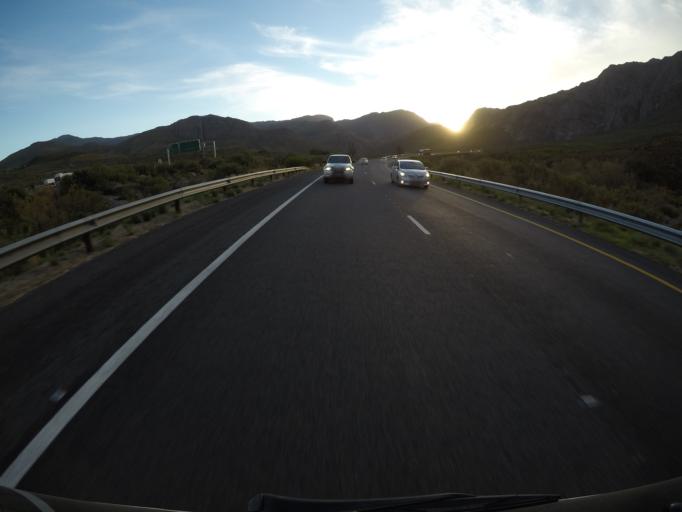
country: ZA
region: Western Cape
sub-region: Cape Winelands District Municipality
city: Paarl
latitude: -33.7265
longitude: 19.1386
